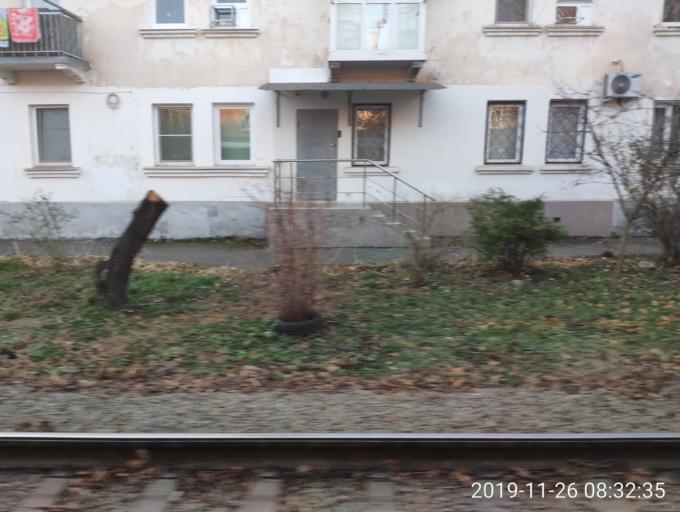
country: RU
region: Krasnodarskiy
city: Krasnodar
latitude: 45.0522
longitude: 38.9930
